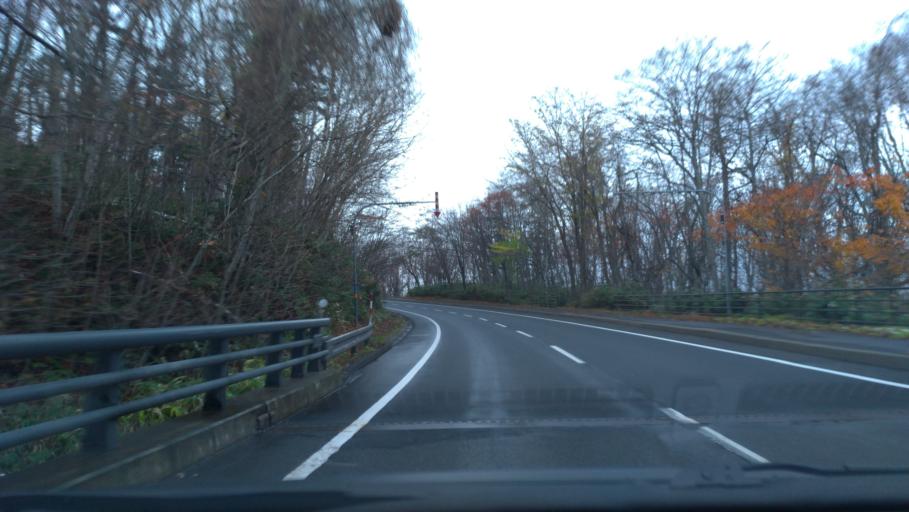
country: JP
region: Hokkaido
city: Shiraoi
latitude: 42.7372
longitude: 141.3595
